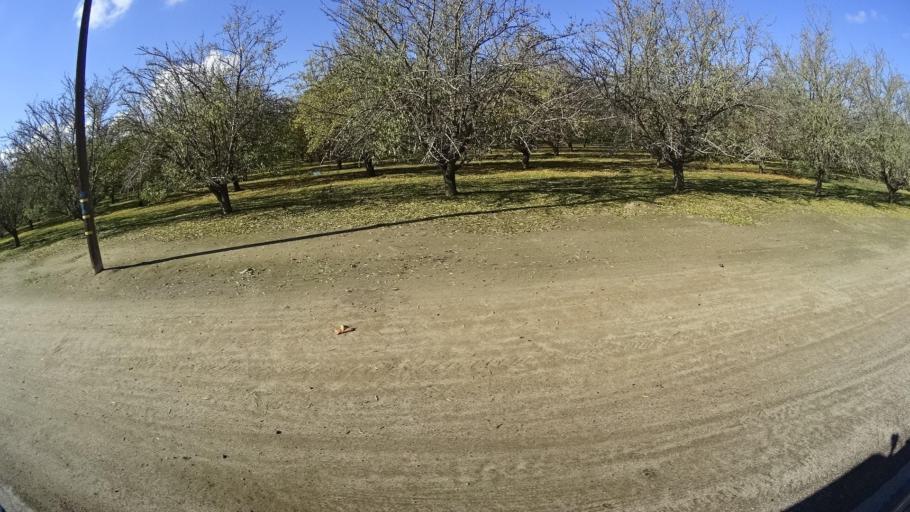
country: US
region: California
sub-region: Kern County
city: McFarland
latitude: 35.6911
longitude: -119.2587
